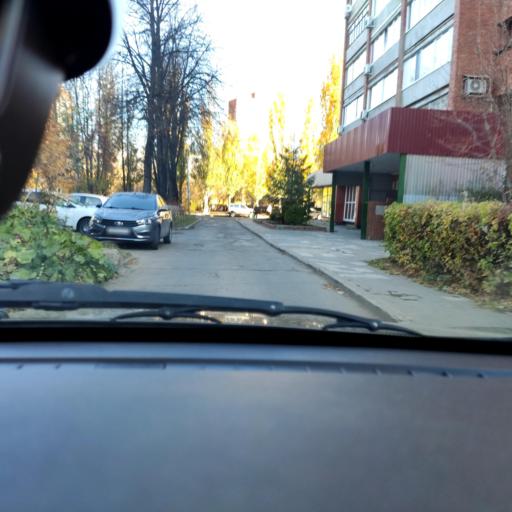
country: RU
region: Samara
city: Tol'yatti
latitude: 53.5230
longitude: 49.2870
